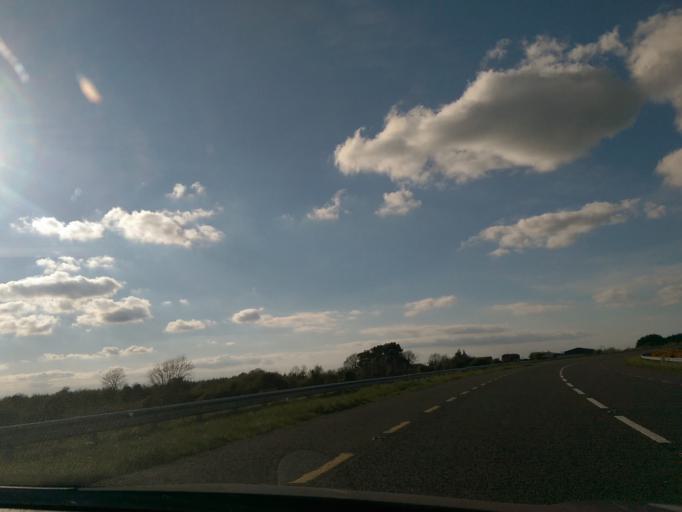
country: IE
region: Connaught
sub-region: County Galway
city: Loughrea
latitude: 53.2578
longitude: -8.6037
